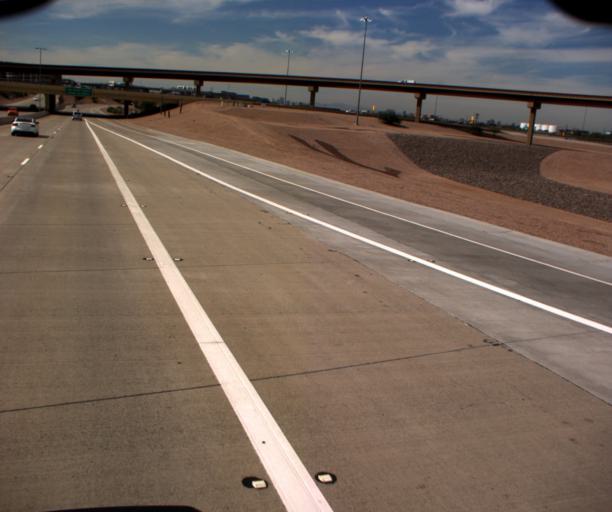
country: US
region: Arizona
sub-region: Maricopa County
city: Tempe Junction
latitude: 33.4369
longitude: -111.9767
